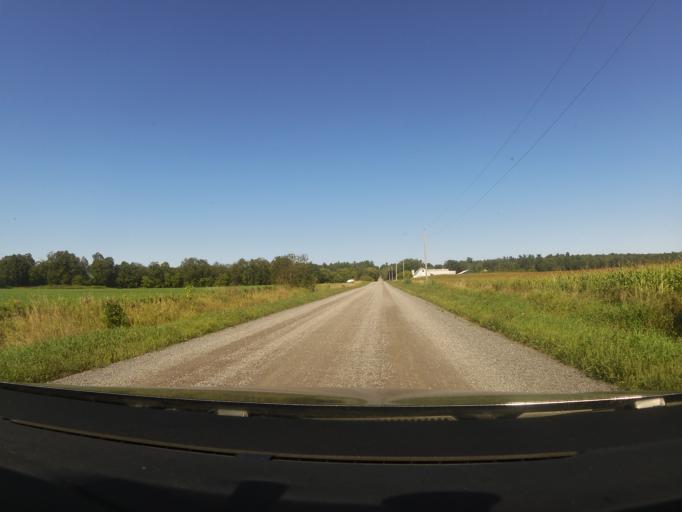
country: CA
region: Ontario
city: Arnprior
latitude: 45.3884
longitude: -76.1347
